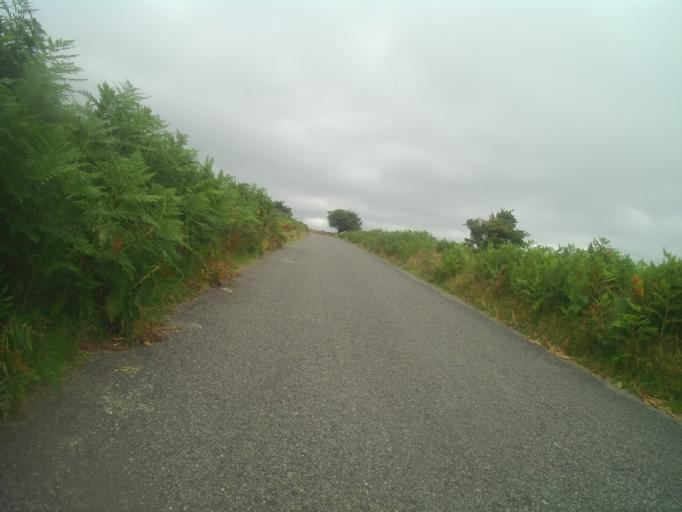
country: GB
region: England
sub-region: Devon
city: Buckfastleigh
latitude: 50.5200
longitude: -3.8470
